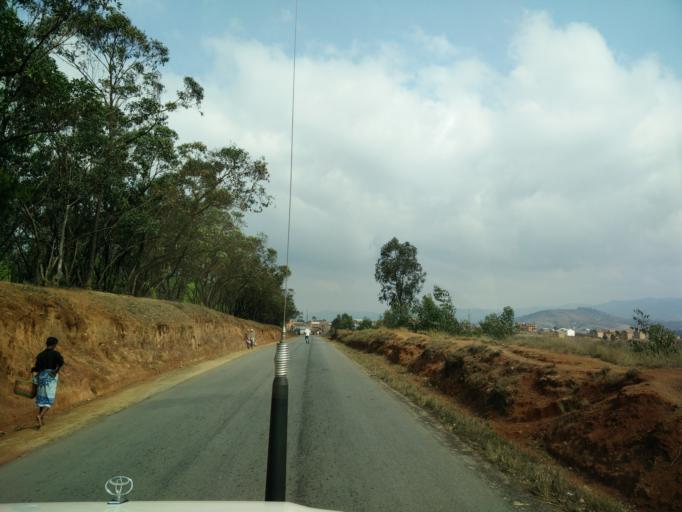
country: MG
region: Upper Matsiatra
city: Fianarantsoa
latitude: -21.3796
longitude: 47.1706
